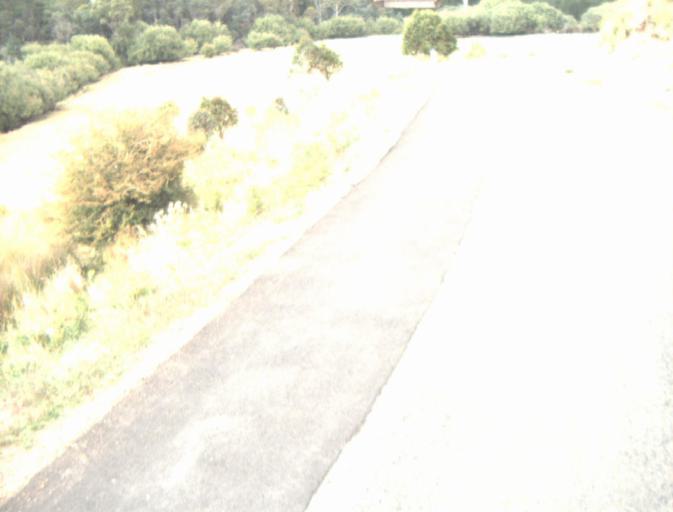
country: AU
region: Tasmania
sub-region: Dorset
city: Scottsdale
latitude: -41.4641
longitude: 147.5940
